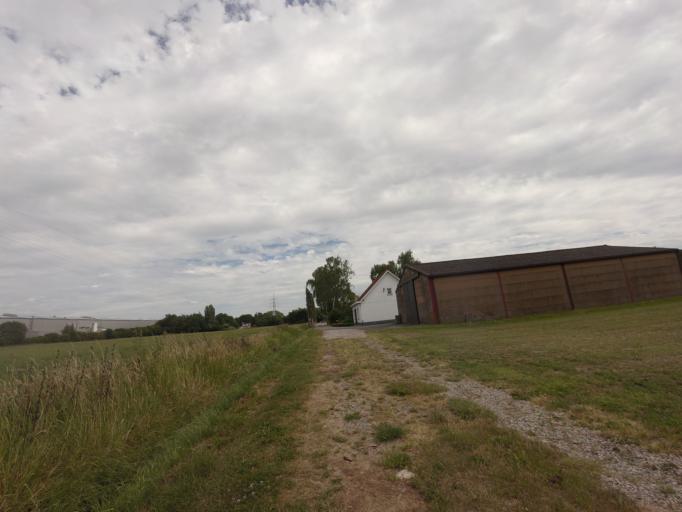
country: BE
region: Flanders
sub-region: Provincie Antwerpen
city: Duffel
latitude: 51.0840
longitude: 4.4705
